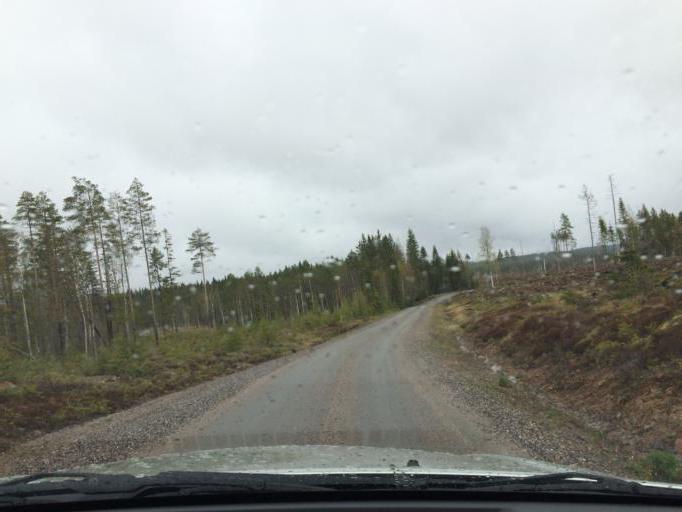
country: SE
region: Dalarna
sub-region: Ludvika Kommun
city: Abborrberget
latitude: 60.0174
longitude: 14.5959
